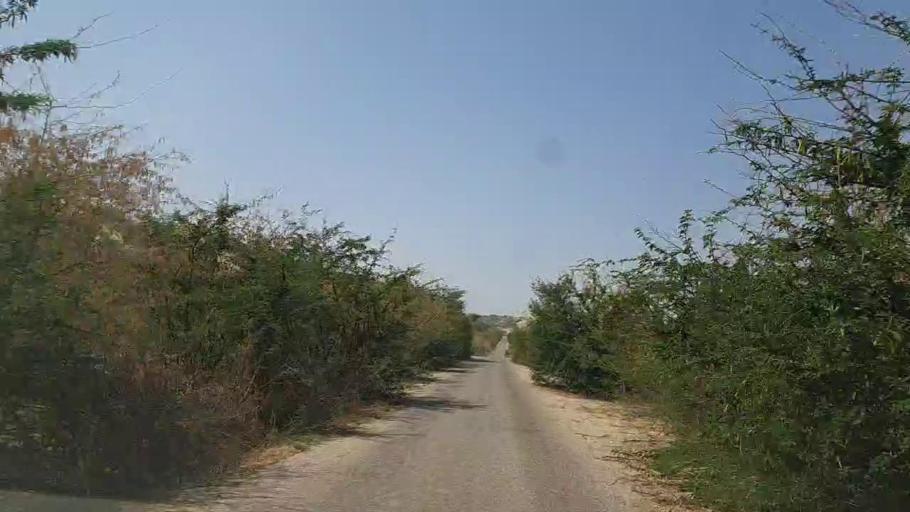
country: PK
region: Sindh
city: Diplo
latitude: 24.5260
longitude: 69.3704
